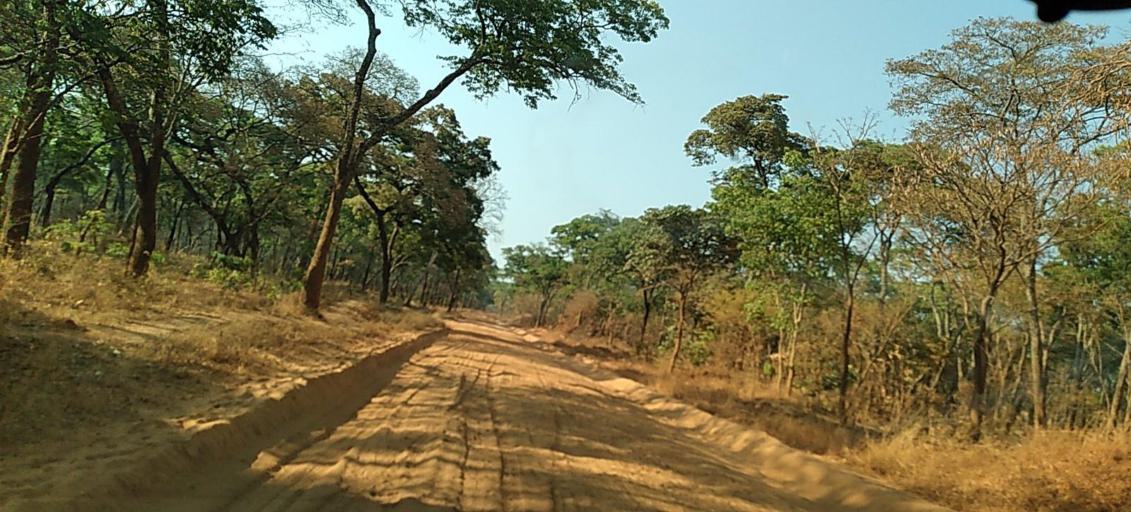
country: ZM
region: North-Western
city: Kasempa
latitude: -13.6096
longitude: 25.9782
